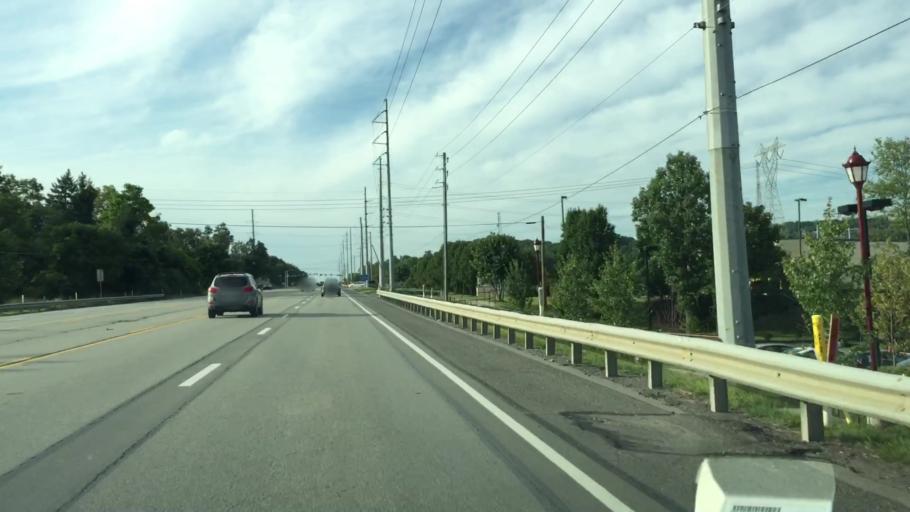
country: US
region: Pennsylvania
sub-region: Butler County
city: Fox Run
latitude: 40.7178
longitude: -80.1047
